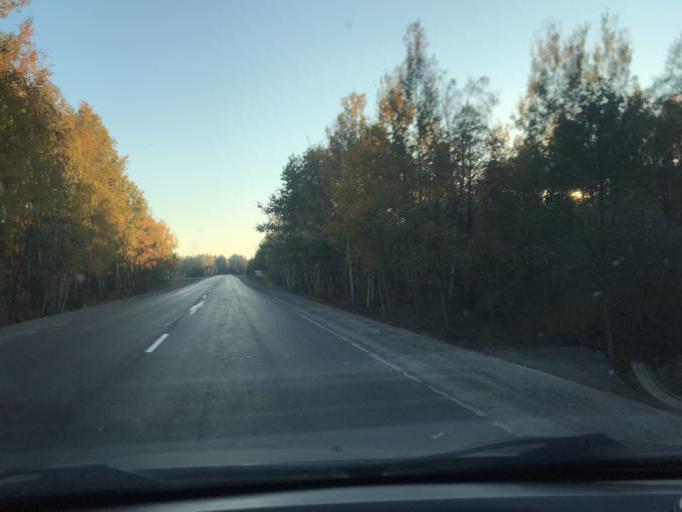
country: BY
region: Gomel
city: Brahin
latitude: 51.8634
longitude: 30.3724
